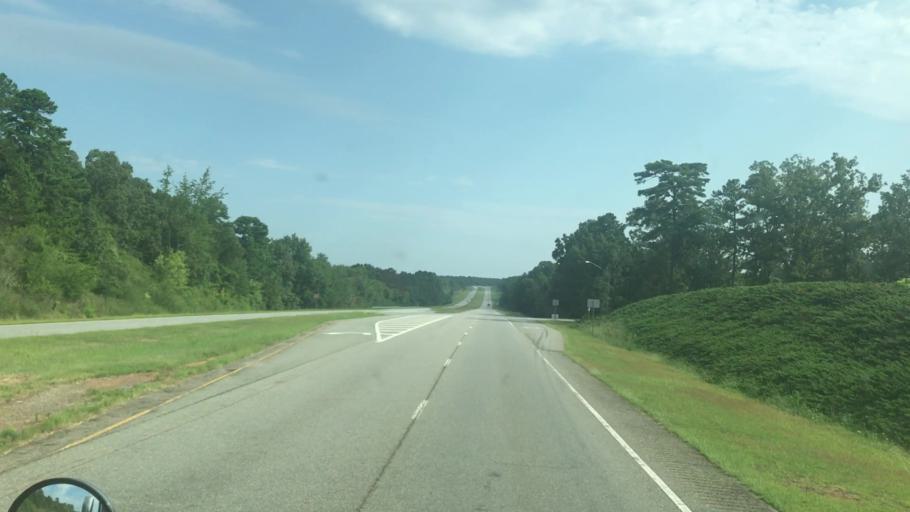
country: US
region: Georgia
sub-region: Early County
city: Blakely
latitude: 31.3957
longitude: -84.9241
